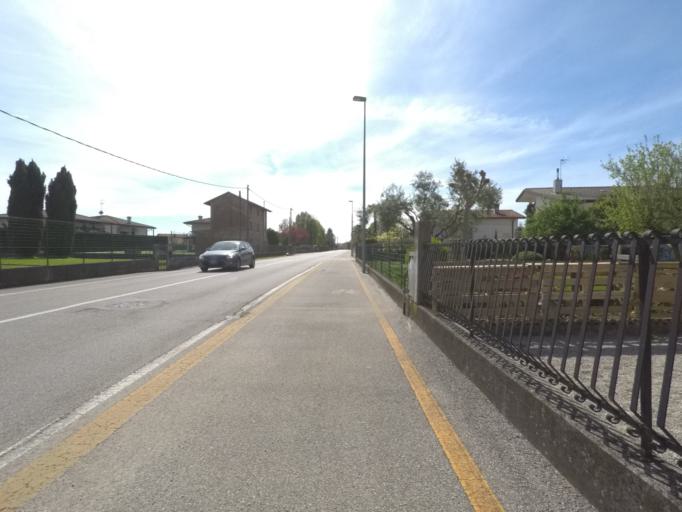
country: IT
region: Friuli Venezia Giulia
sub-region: Provincia di Pordenone
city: Orcenico Inferiore
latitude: 45.9435
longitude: 12.7584
